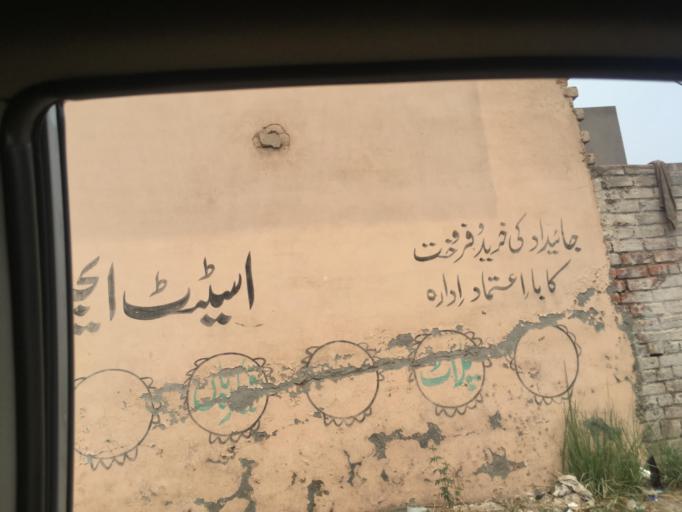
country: PK
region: Punjab
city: Lahore
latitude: 31.6189
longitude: 74.3539
